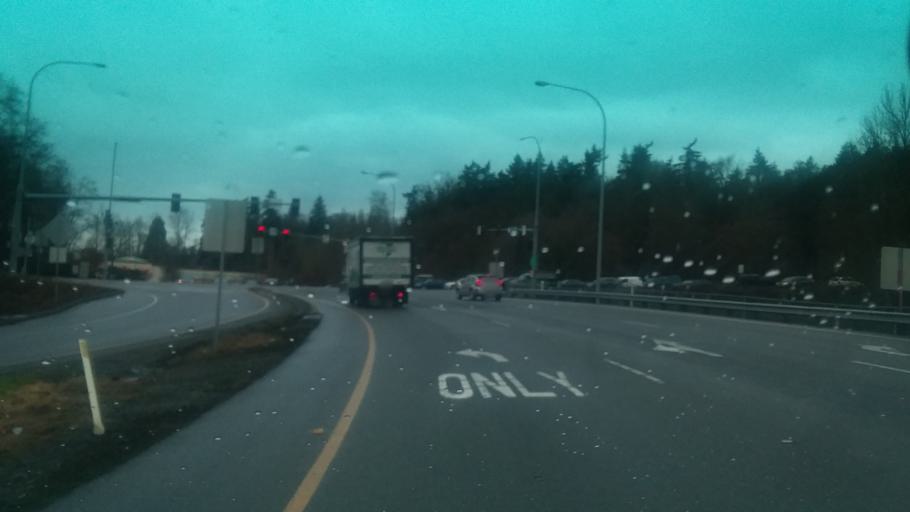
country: US
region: Washington
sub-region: King County
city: Kent
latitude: 47.4114
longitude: -122.2187
